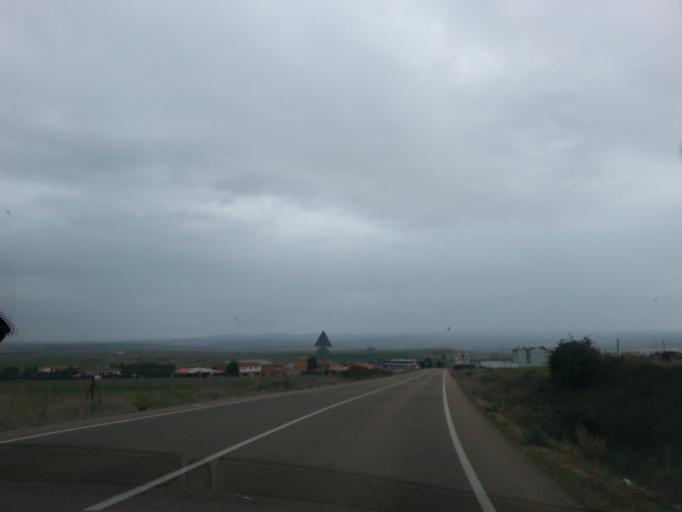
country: ES
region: Castille and Leon
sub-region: Provincia de Salamanca
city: Tamames
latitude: 40.6585
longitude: -6.1174
